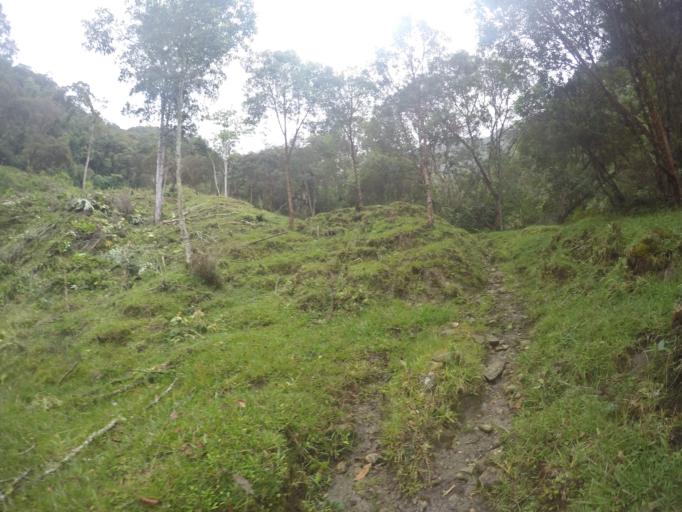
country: CO
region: Tolima
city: Cajamarca
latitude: 4.5286
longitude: -75.3552
